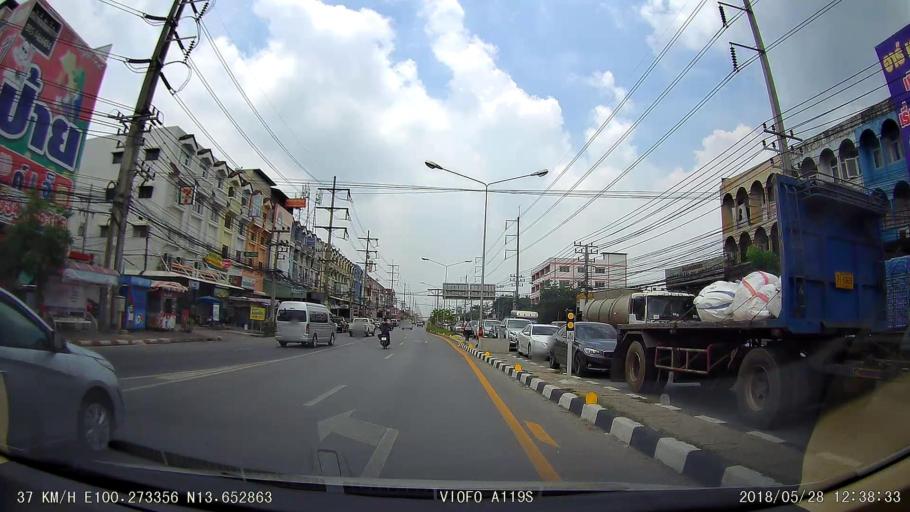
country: TH
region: Samut Sakhon
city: Krathum Baen
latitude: 13.6528
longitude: 100.2736
